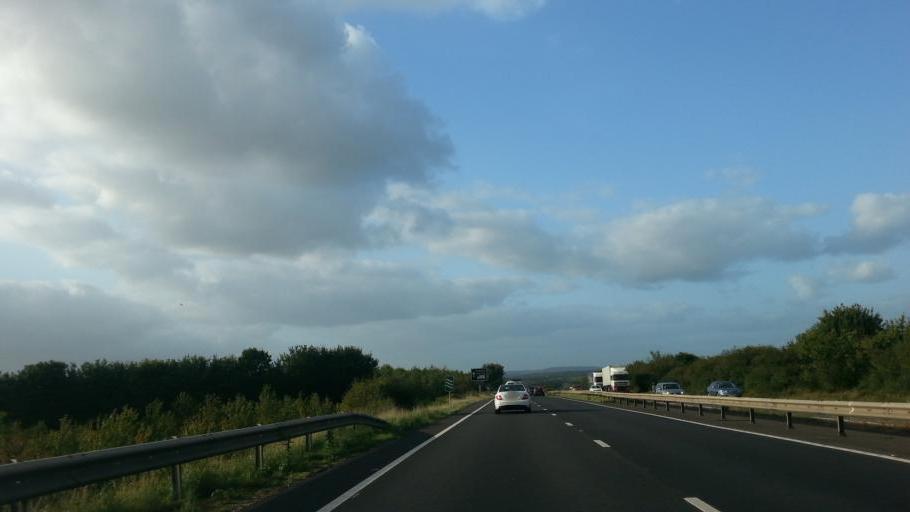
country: GB
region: England
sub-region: Hampshire
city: Overton
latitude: 51.2102
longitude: -1.3406
